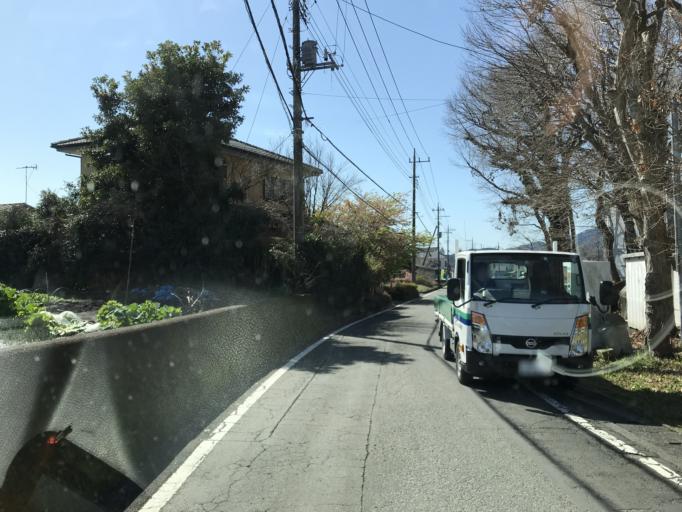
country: JP
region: Shizuoka
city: Fujinomiya
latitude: 35.2224
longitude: 138.6460
